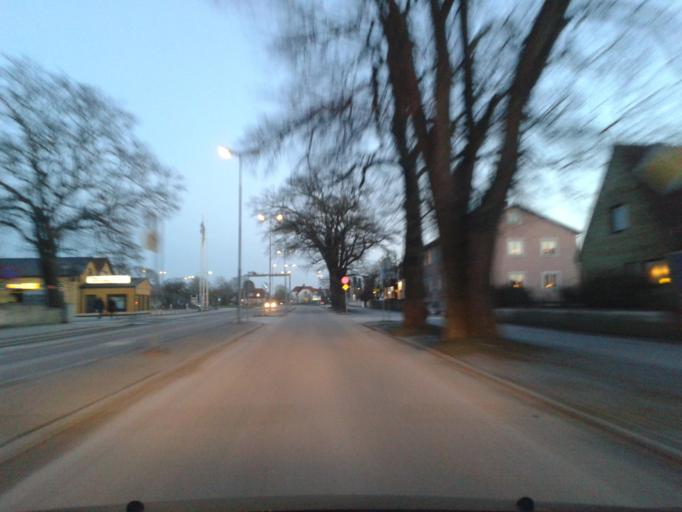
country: SE
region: Gotland
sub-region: Gotland
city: Visby
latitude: 57.6361
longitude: 18.3042
